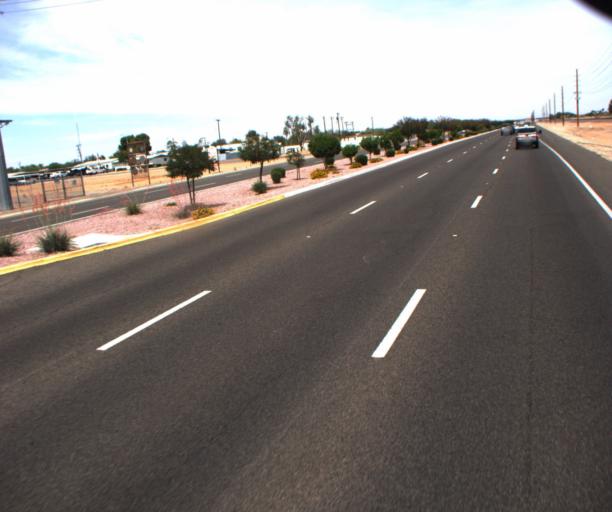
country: US
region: Arizona
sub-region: Maricopa County
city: Sun City West
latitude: 33.6607
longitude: -112.3783
